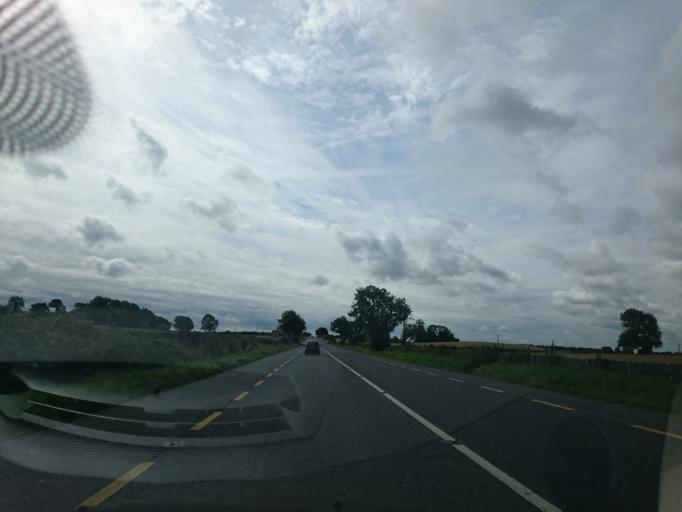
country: IE
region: Leinster
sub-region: Kilkenny
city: Kilkenny
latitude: 52.6203
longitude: -7.2490
